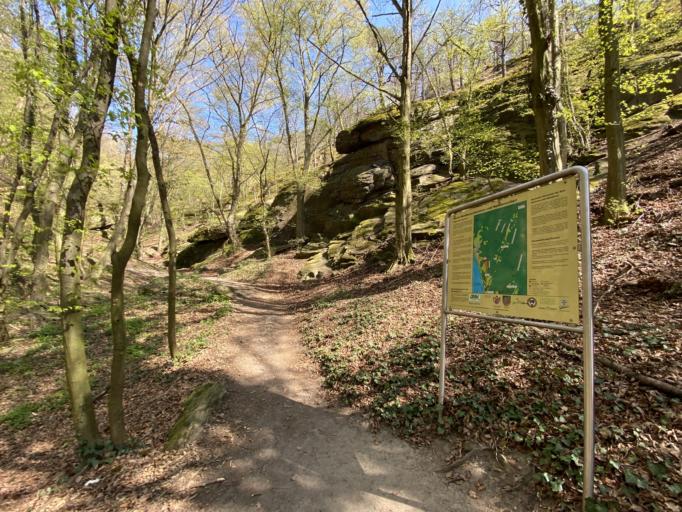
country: AT
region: Lower Austria
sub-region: Politischer Bezirk Krems
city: Durnstein
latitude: 48.4008
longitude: 15.5210
